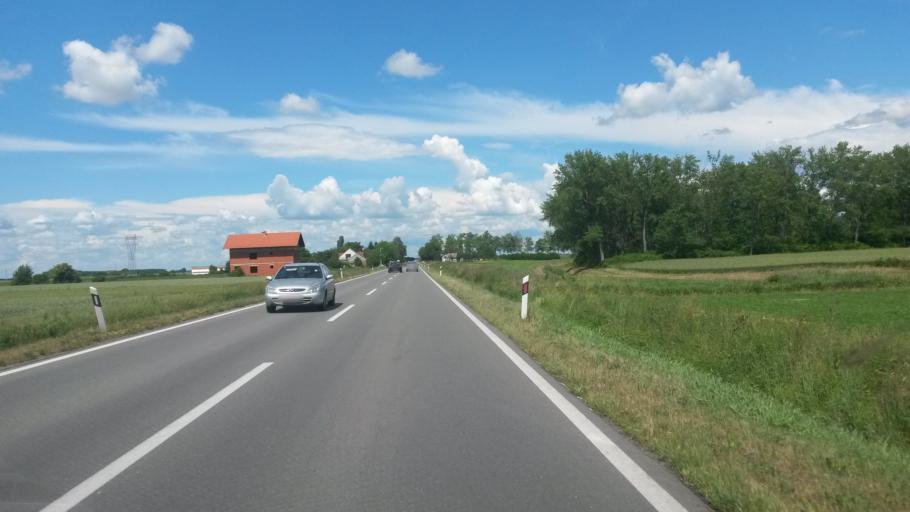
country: HR
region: Osjecko-Baranjska
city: Vuka
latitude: 45.4525
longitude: 18.5111
